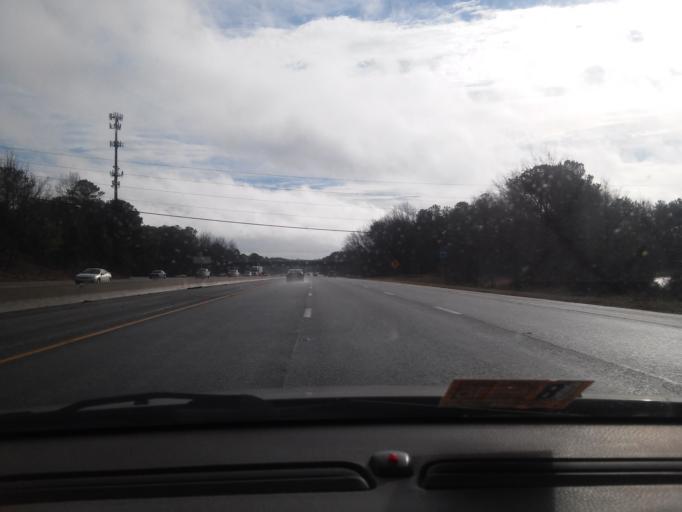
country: US
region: Virginia
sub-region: Henrico County
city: Tuckahoe
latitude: 37.6256
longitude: -77.5572
